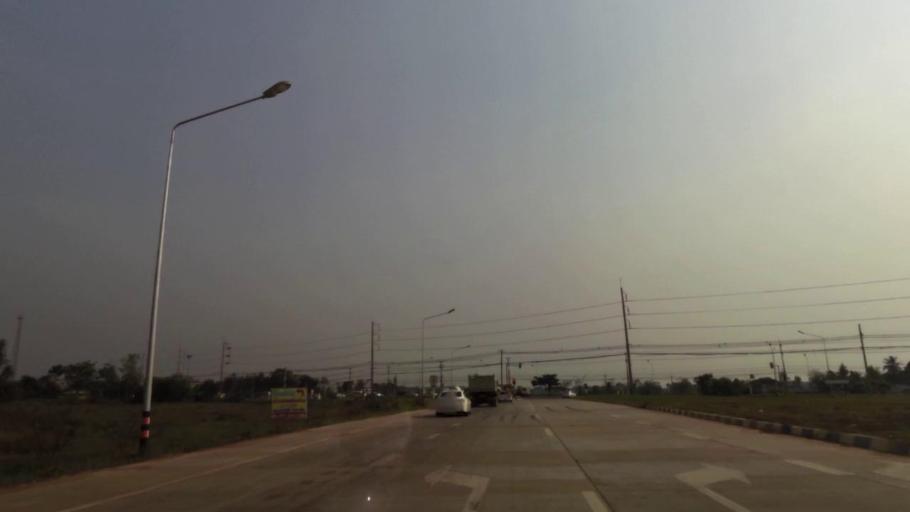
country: TH
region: Rayong
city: Klaeng
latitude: 12.7865
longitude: 101.6774
